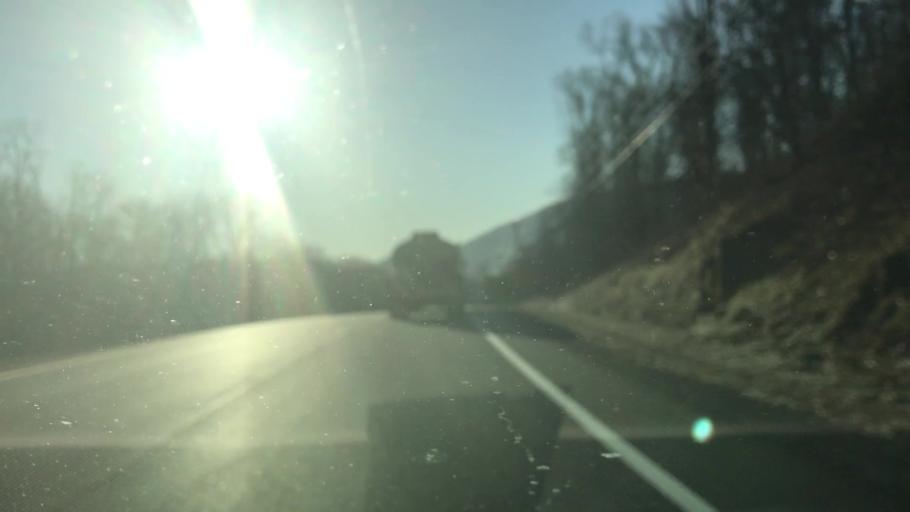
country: US
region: Virginia
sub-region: Botetourt County
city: Blue Ridge
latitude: 37.3929
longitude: -79.7450
